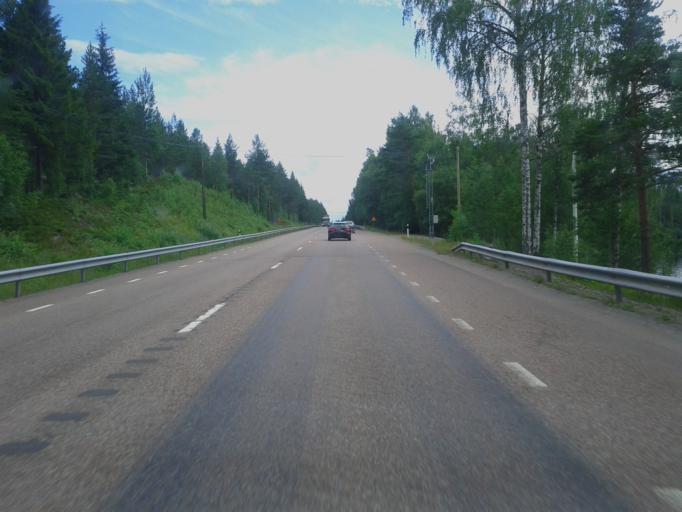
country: SE
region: Dalarna
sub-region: Faluns Kommun
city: Bjursas
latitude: 60.7142
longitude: 15.4604
